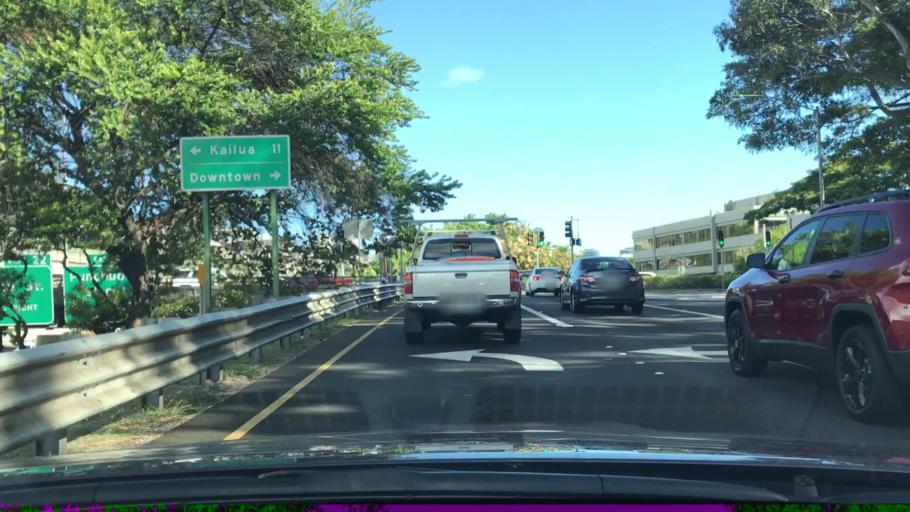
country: US
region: Hawaii
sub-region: Honolulu County
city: Honolulu
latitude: 21.3148
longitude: -157.8552
